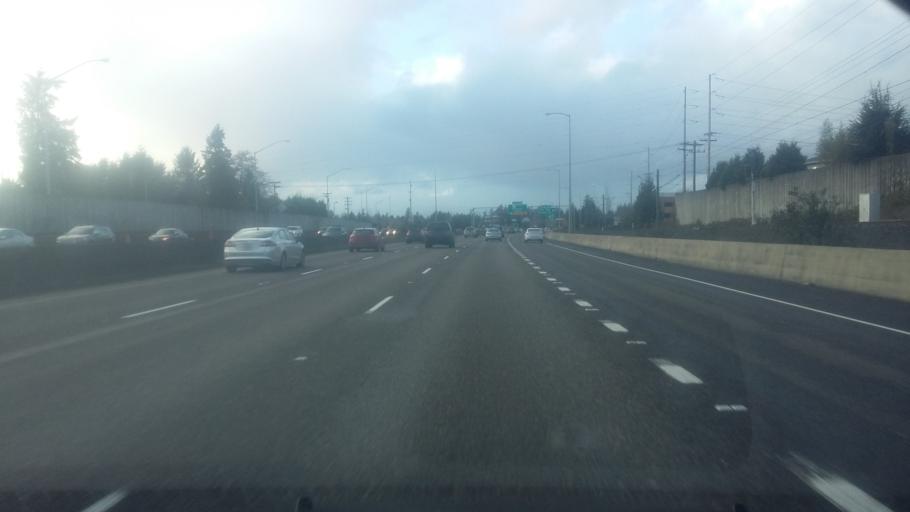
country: US
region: Oregon
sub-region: Washington County
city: West Haven-Sylvan
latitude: 45.5067
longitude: -122.7708
